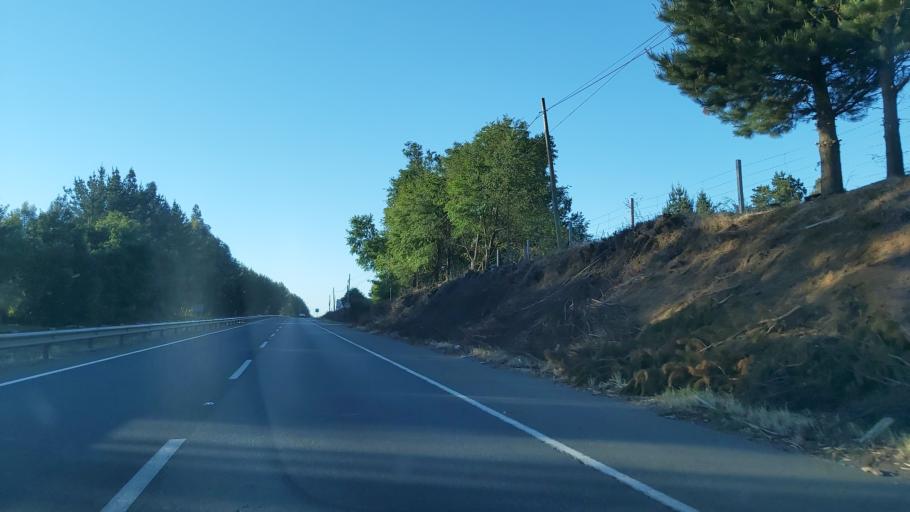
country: CL
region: Araucania
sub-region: Provincia de Malleco
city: Collipulli
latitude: -38.0767
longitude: -72.3717
